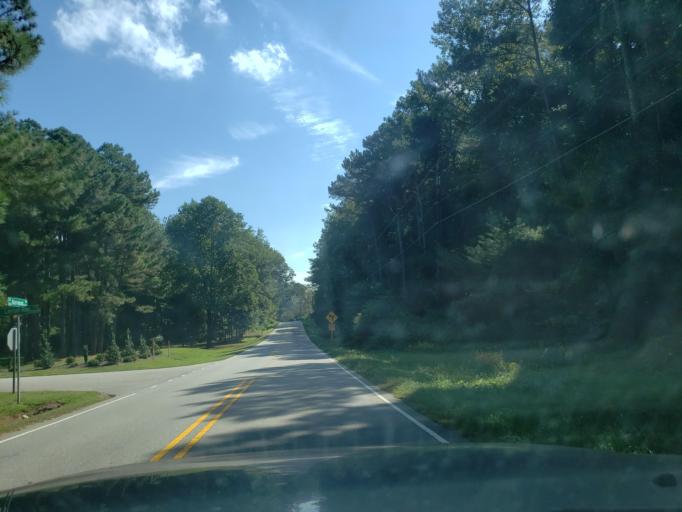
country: US
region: North Carolina
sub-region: Wake County
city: West Raleigh
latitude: 35.9329
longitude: -78.7094
